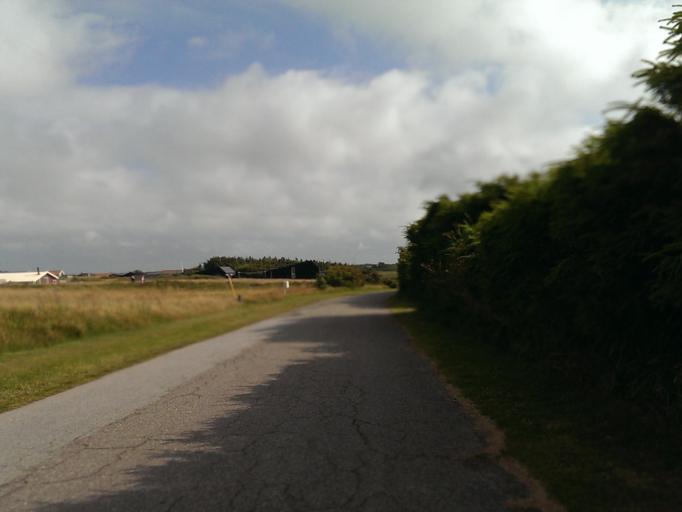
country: DK
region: North Denmark
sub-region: Jammerbugt Kommune
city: Pandrup
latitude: 57.3893
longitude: 9.7286
